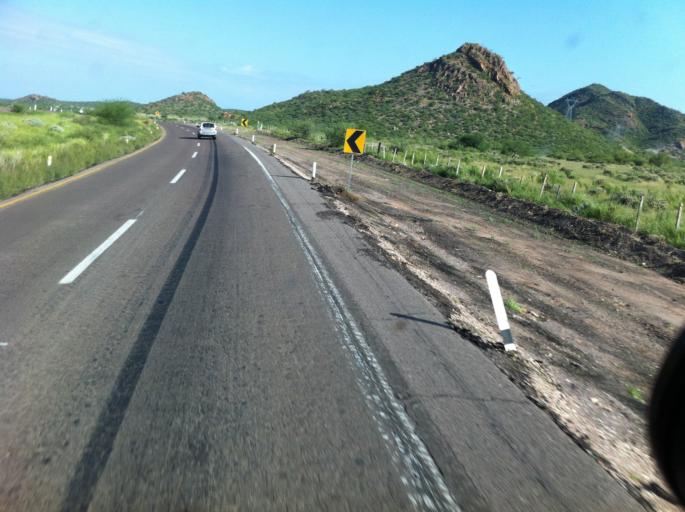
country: MX
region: Sonora
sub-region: Empalme
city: La Palma
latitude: 28.4506
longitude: -111.0456
